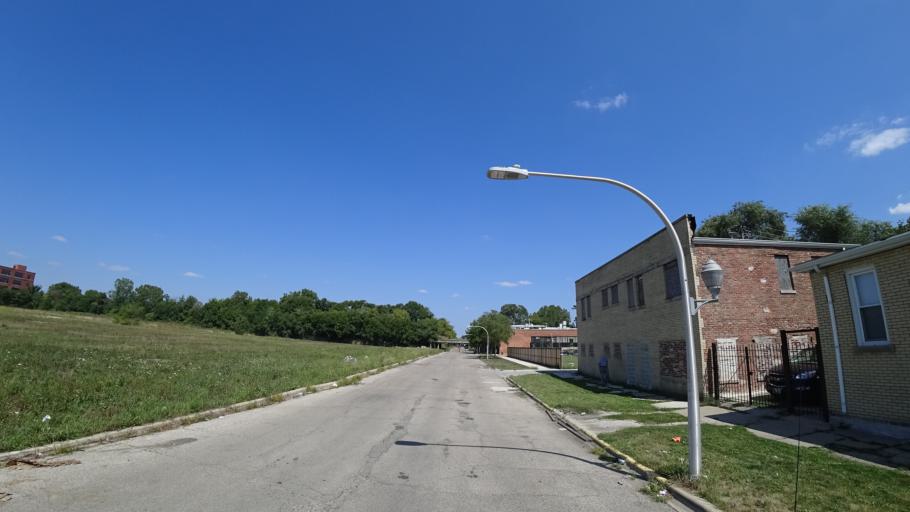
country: US
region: Illinois
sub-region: Cook County
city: Cicero
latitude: 41.8671
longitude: -87.7325
